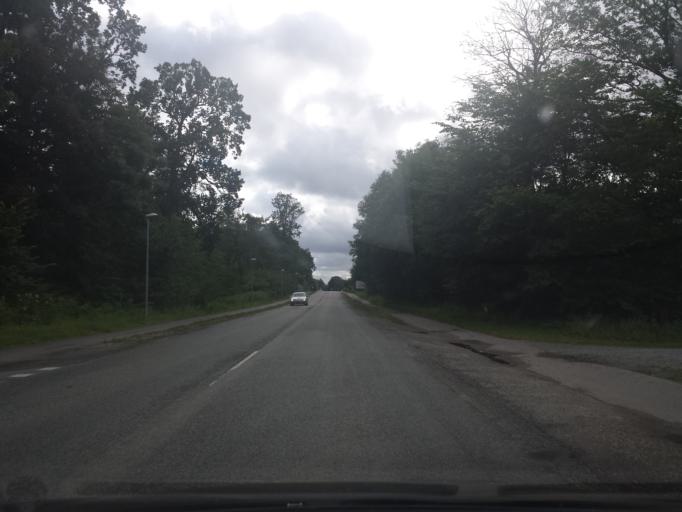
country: DK
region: South Denmark
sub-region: Sonderborg Kommune
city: Grasten
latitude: 54.9300
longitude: 9.6049
